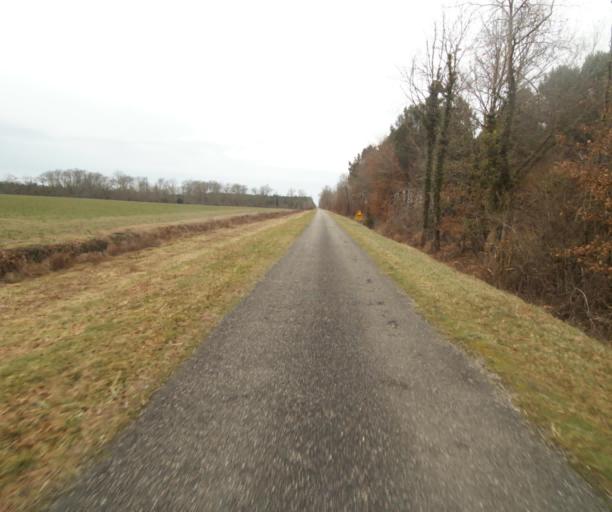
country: FR
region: Aquitaine
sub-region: Departement des Landes
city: Gabarret
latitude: 44.0163
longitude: -0.0373
